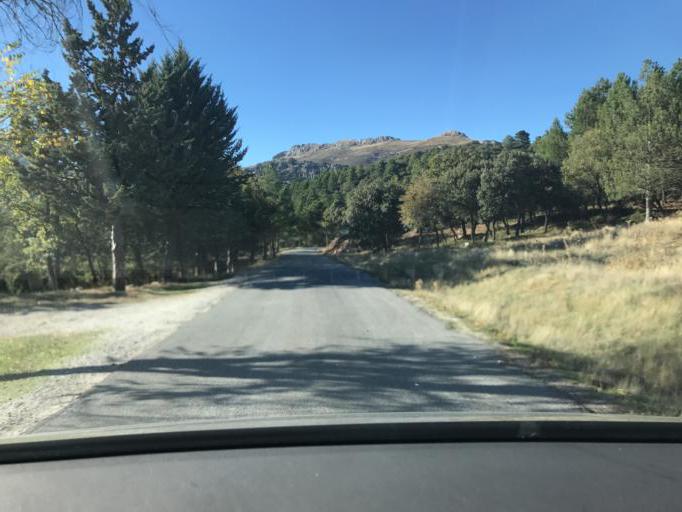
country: ES
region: Andalusia
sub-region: Provincia de Granada
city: Beas de Granada
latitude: 37.3055
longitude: -3.4528
